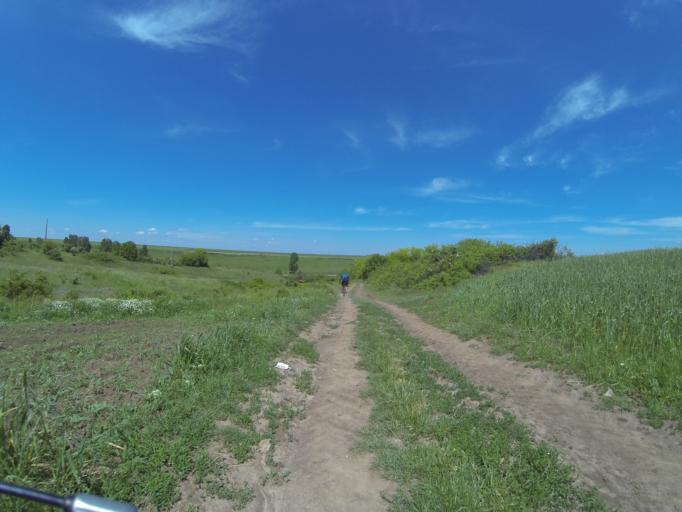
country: RO
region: Dolj
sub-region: Comuna Teslui
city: Teslui
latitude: 44.1989
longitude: 24.1416
